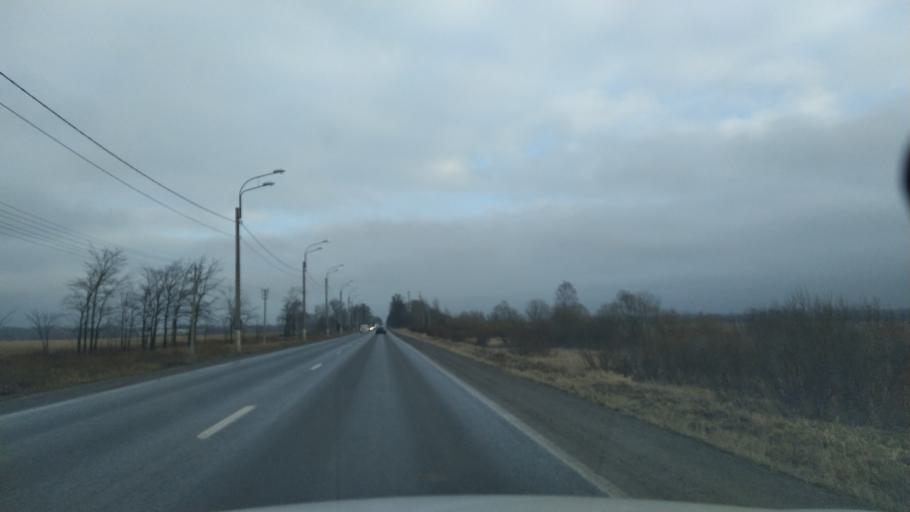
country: RU
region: St.-Petersburg
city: Aleksandrovskaya
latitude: 59.7112
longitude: 30.3151
